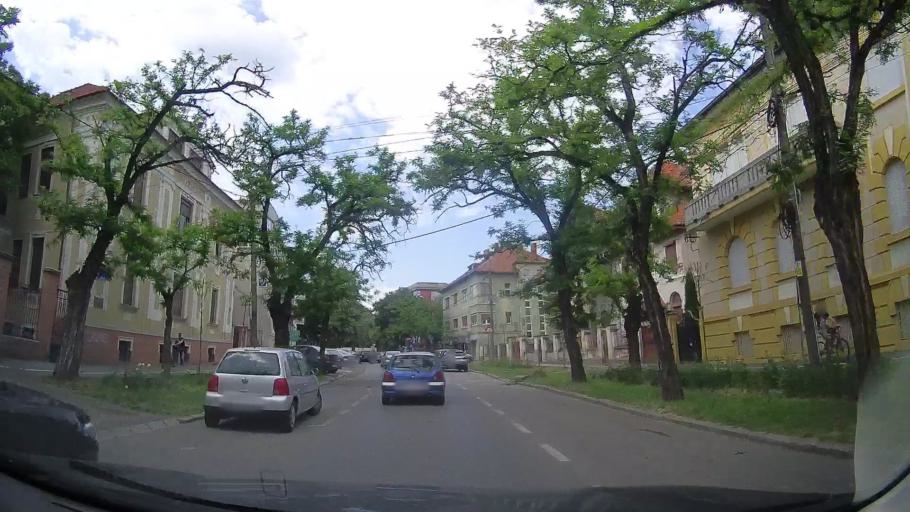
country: RO
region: Timis
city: Timisoara
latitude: 45.7548
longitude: 21.2369
